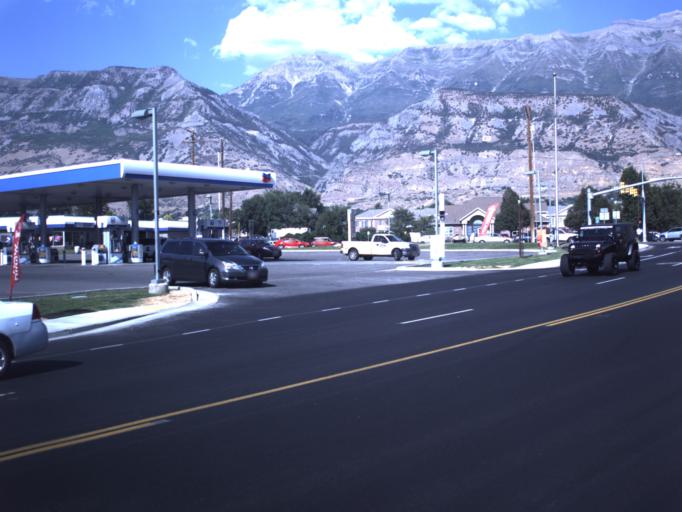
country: US
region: Utah
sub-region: Utah County
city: Pleasant Grove
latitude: 40.3514
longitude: -111.7329
